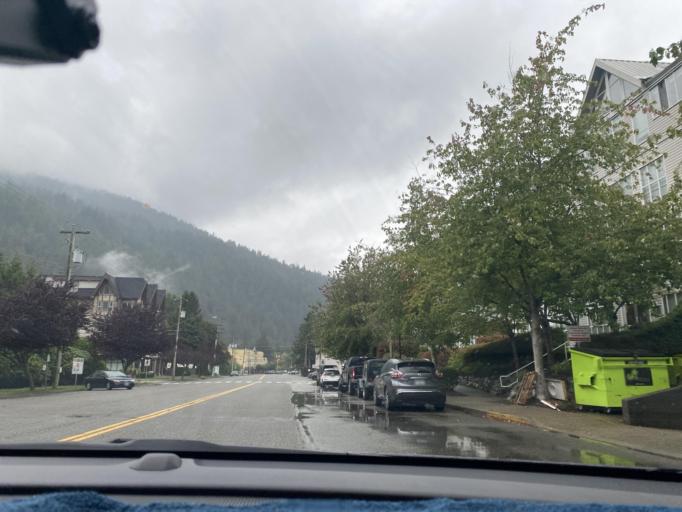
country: CA
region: British Columbia
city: Agassiz
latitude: 49.3025
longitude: -121.7817
